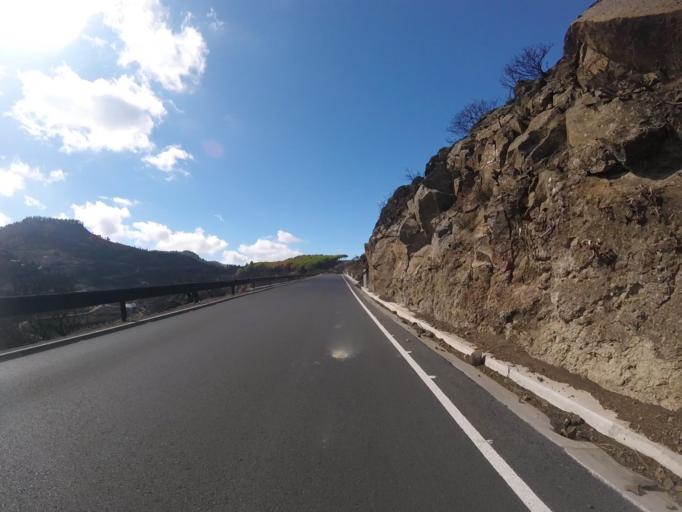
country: ES
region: Canary Islands
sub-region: Provincia de Las Palmas
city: Tejeda
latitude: 27.9905
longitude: -15.5920
